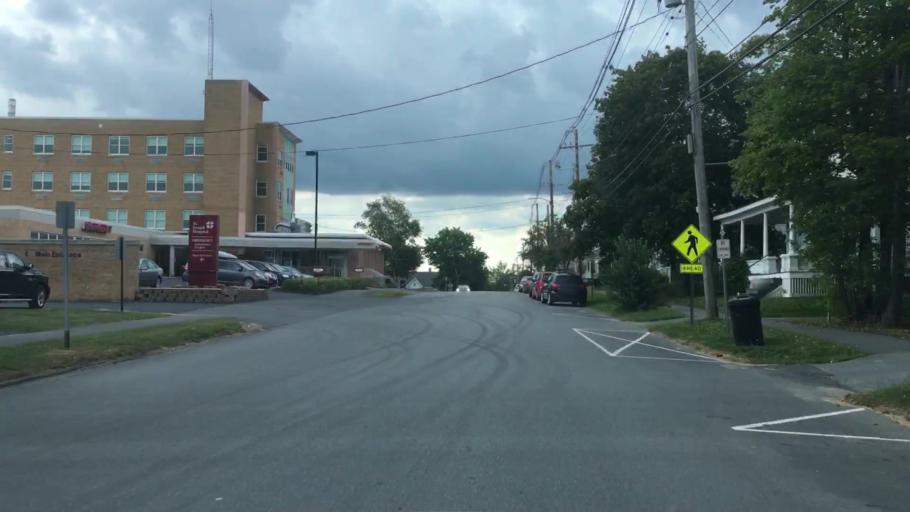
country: US
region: Maine
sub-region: Penobscot County
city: Bangor
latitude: 44.8149
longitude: -68.7735
